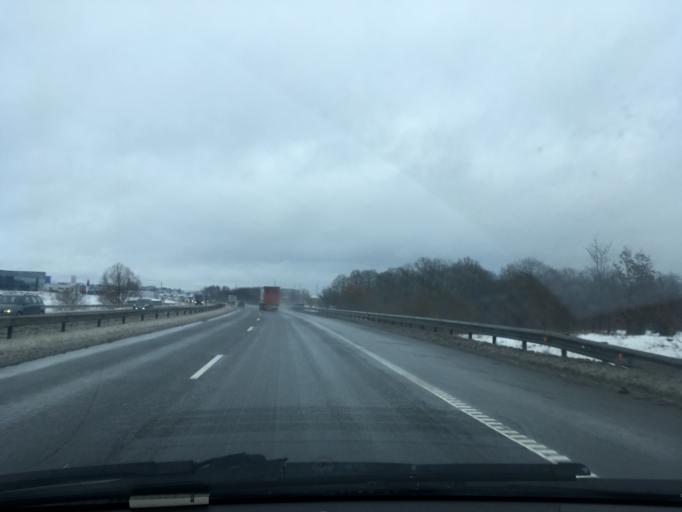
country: LT
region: Kauno apskritis
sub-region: Kaunas
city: Silainiai
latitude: 54.9306
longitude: 23.8632
